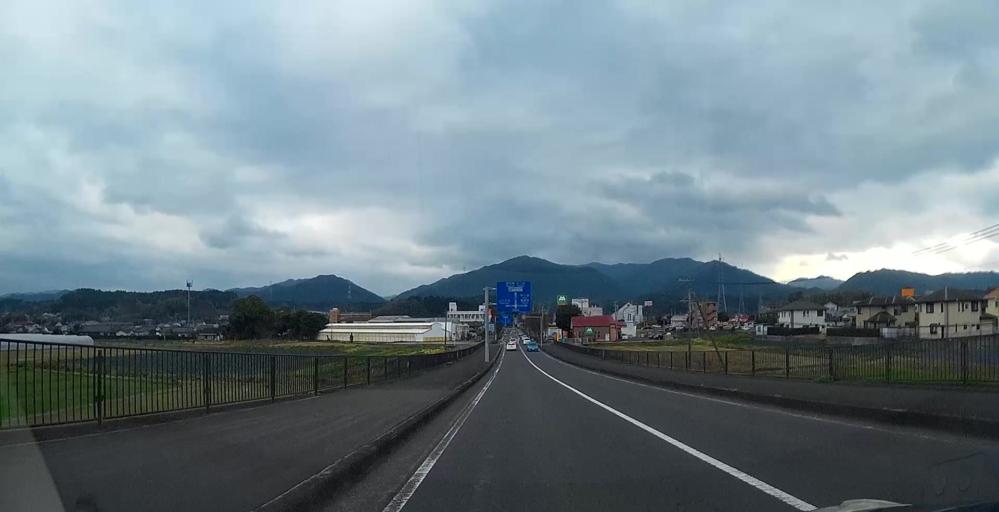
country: JP
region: Kagoshima
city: Izumi
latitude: 32.0761
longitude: 130.3471
